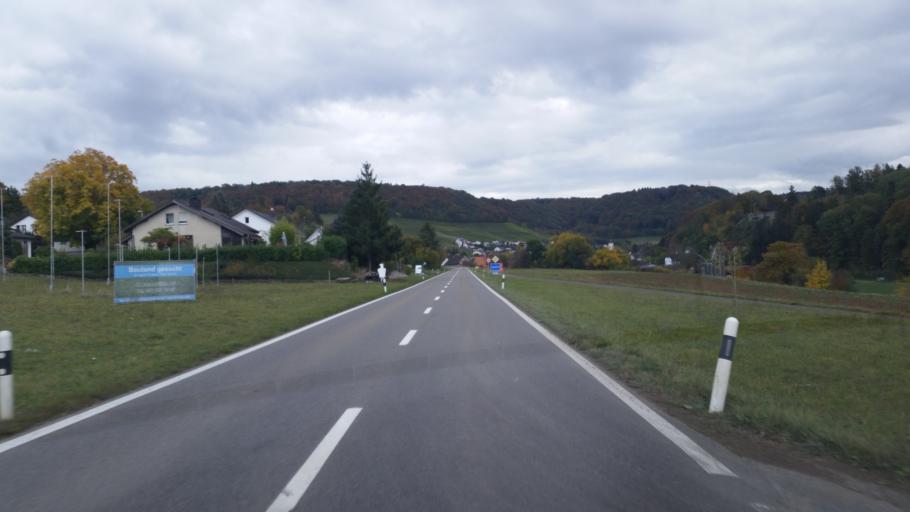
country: CH
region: Aargau
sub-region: Bezirk Zurzach
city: Tegerfelden
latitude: 47.5630
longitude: 8.2790
